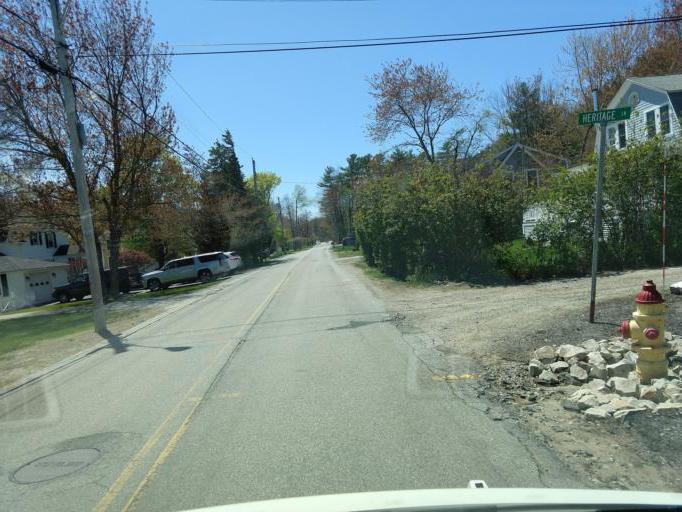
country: US
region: Maine
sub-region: York County
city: Ogunquit
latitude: 43.2427
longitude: -70.6039
